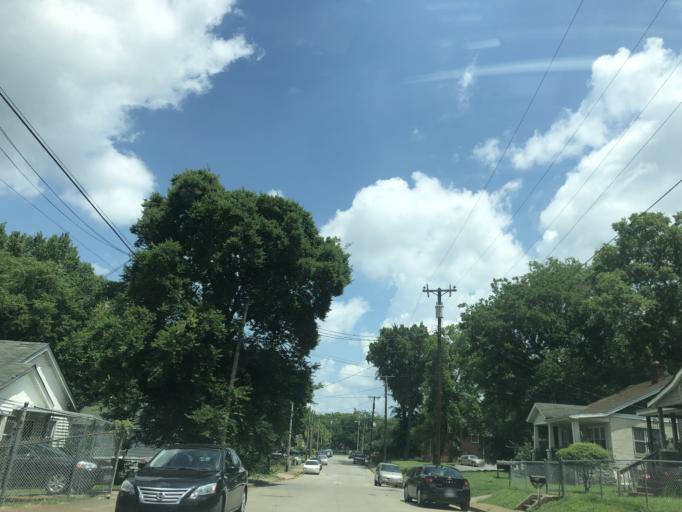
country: US
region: Tennessee
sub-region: Davidson County
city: Nashville
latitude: 36.1582
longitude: -86.8210
